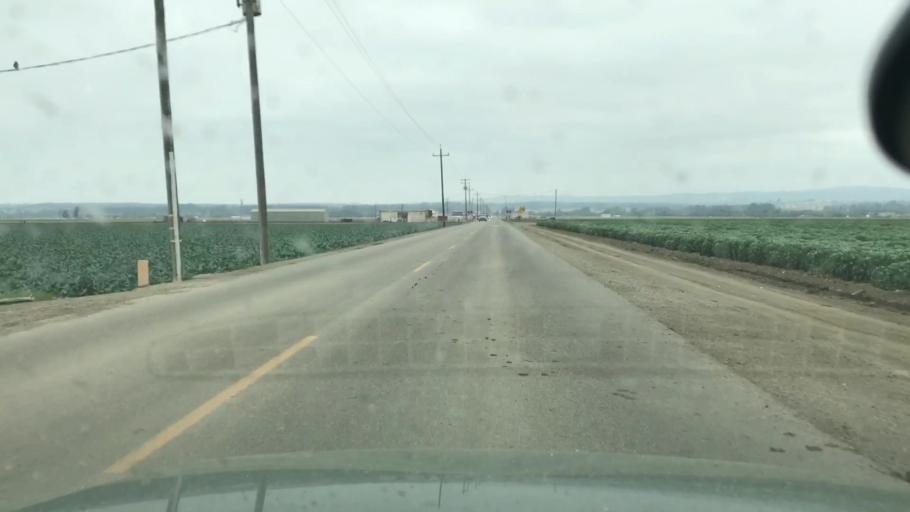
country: US
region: California
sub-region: Santa Barbara County
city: Lompoc
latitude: 34.6443
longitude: -120.4931
